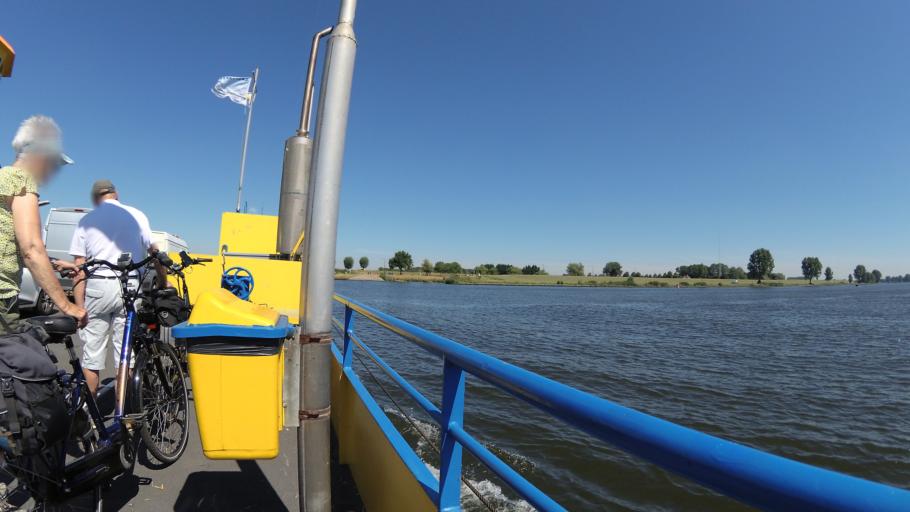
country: NL
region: North Brabant
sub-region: Gemeente Waalwijk
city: Waalwijk
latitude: 51.7108
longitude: 5.0494
